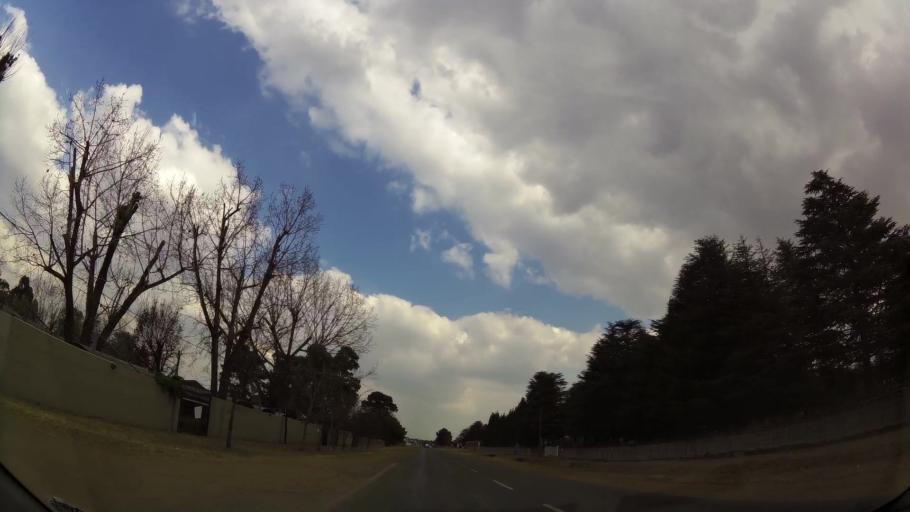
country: ZA
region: Gauteng
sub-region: Ekurhuleni Metropolitan Municipality
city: Benoni
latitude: -26.1243
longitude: 28.3573
